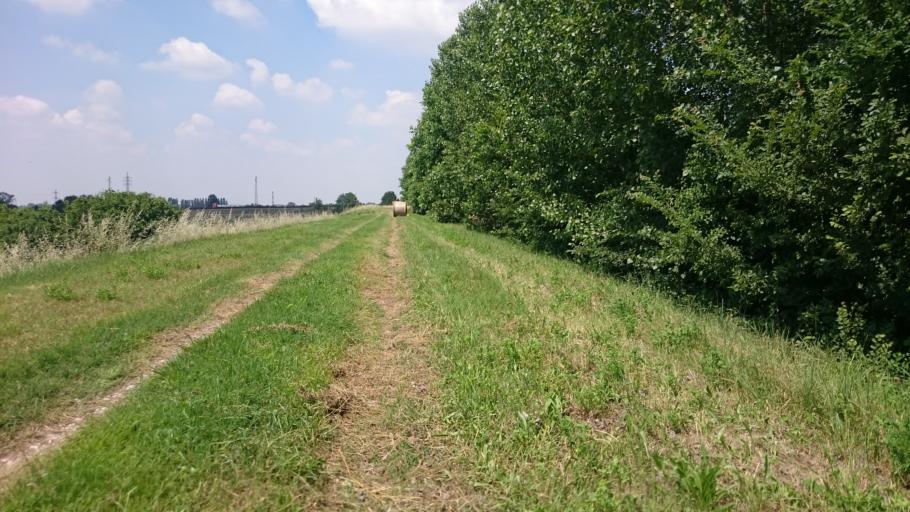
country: IT
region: Lombardy
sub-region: Provincia di Mantova
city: Bagnolo San Vito
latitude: 45.1096
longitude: 10.8683
